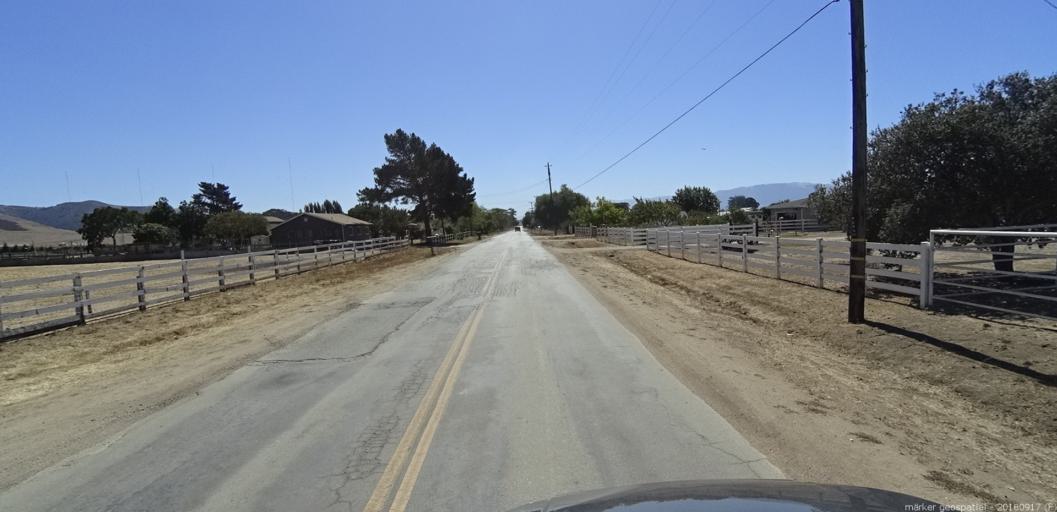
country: US
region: California
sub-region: Monterey County
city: Salinas
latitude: 36.7356
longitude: -121.5990
